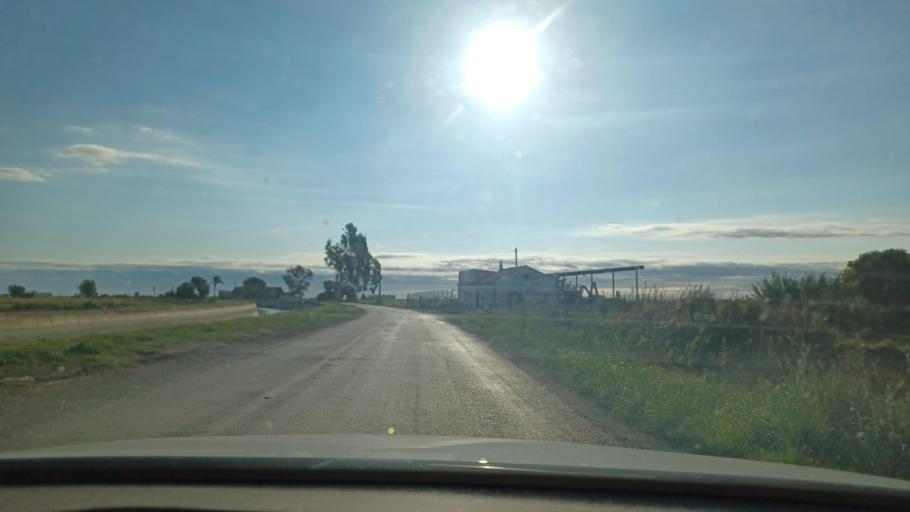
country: ES
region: Catalonia
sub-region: Provincia de Tarragona
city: Amposta
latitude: 40.6991
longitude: 0.6129
